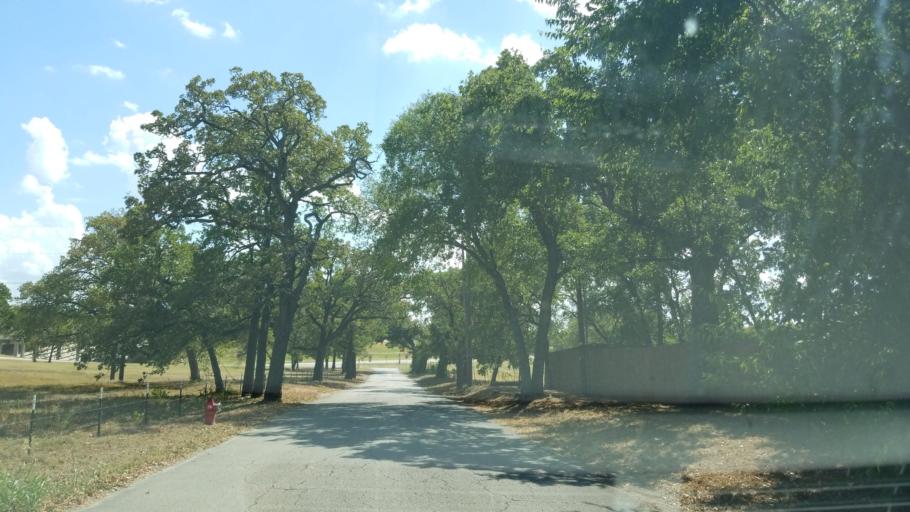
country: US
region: Texas
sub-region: Tarrant County
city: Euless
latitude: 32.8607
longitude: -97.1068
